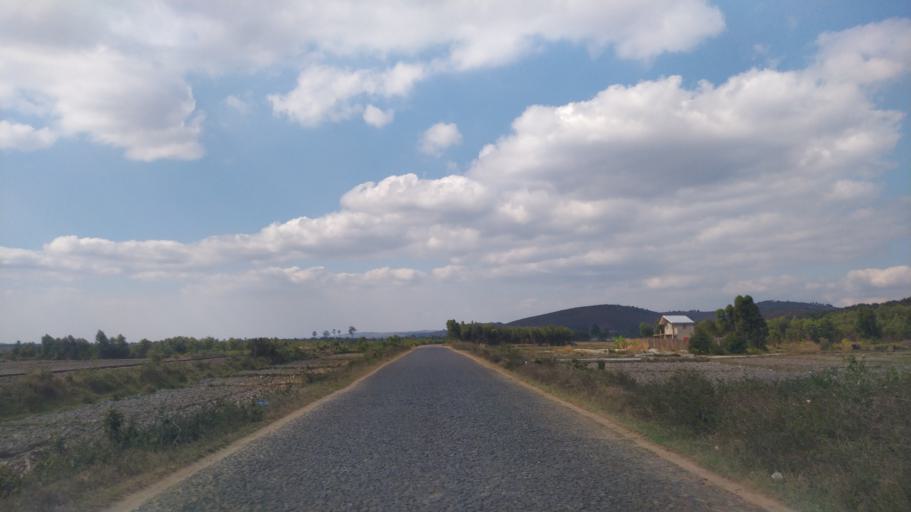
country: MG
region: Alaotra Mangoro
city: Moramanga
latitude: -18.7648
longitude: 48.2545
